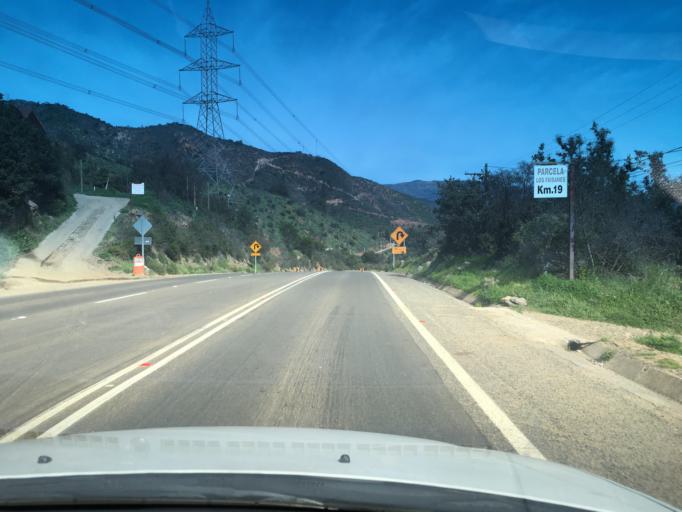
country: CL
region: Valparaiso
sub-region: Provincia de Marga Marga
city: Limache
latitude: -33.0592
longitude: -71.0475
